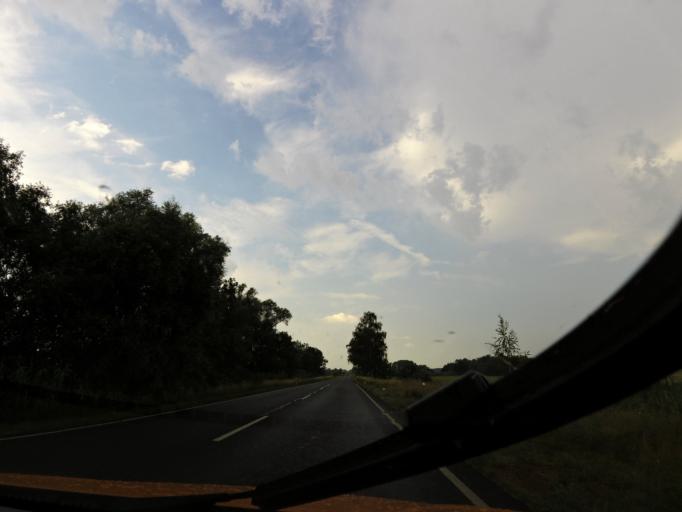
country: DE
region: Brandenburg
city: Friesack
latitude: 52.7754
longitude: 12.5604
